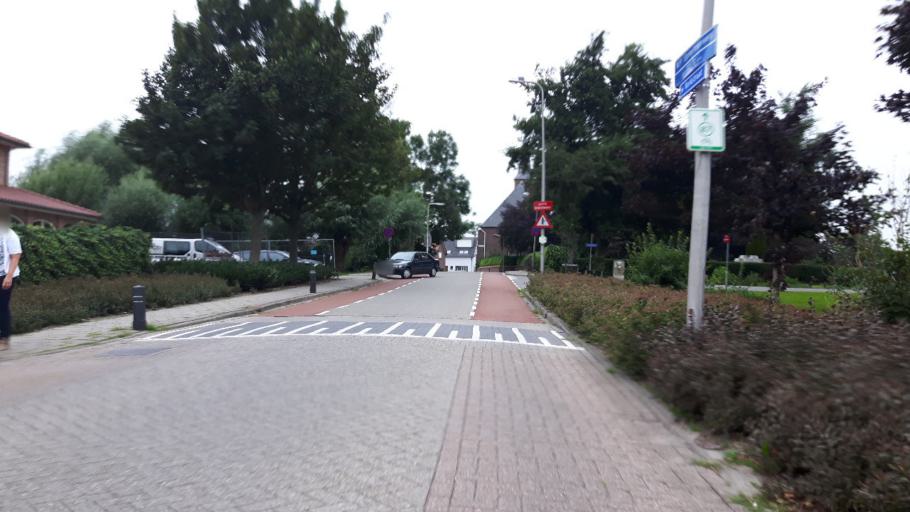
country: NL
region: South Holland
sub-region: Gemeente Nieuwkoop
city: Nieuwkoop
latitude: 52.1951
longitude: 4.7580
